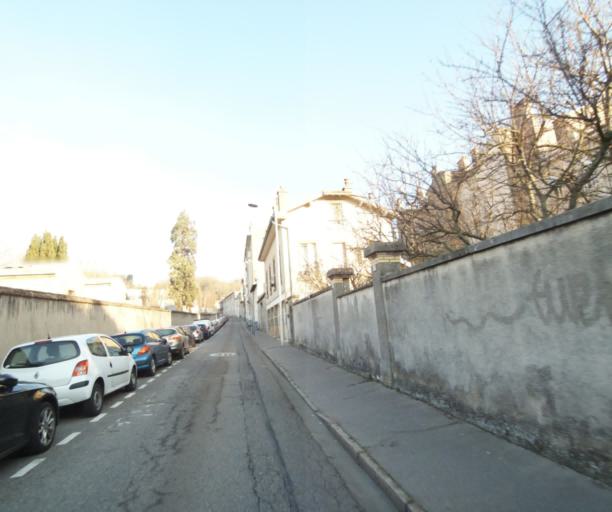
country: FR
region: Lorraine
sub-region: Departement de Meurthe-et-Moselle
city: Maxeville
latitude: 48.6898
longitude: 6.1658
